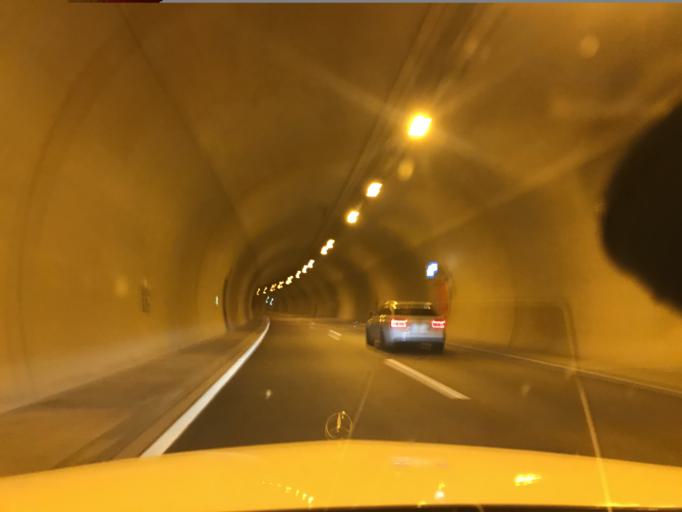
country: DE
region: Hesse
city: Hessisch Lichtenau
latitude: 51.1942
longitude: 9.7659
